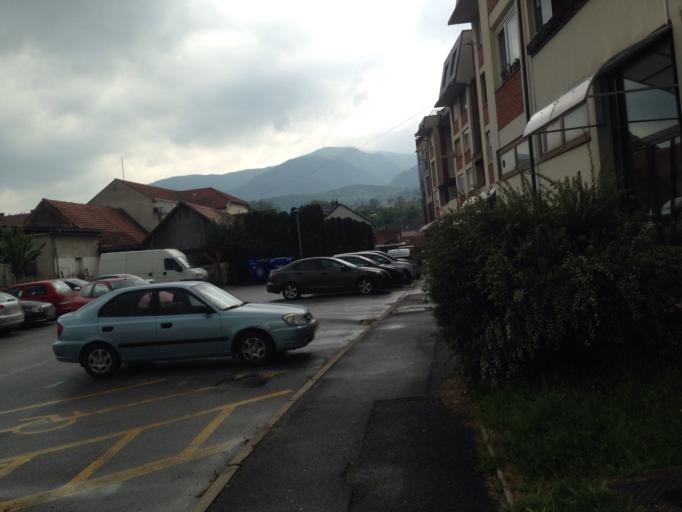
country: HR
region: Varazdinska
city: Ivanec
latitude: 46.2249
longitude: 16.1226
